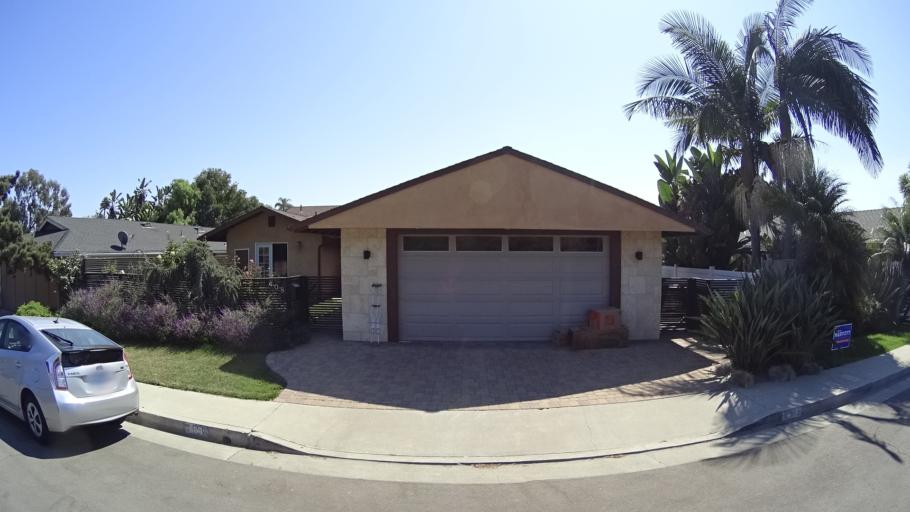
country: US
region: California
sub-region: Orange County
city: San Clemente
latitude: 33.4486
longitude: -117.6418
